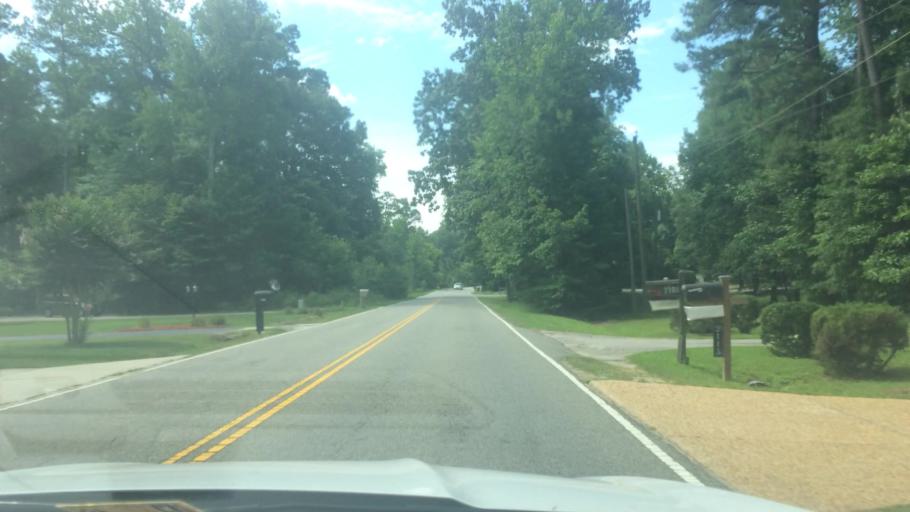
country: US
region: Virginia
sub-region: York County
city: Yorktown
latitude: 37.1663
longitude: -76.4382
